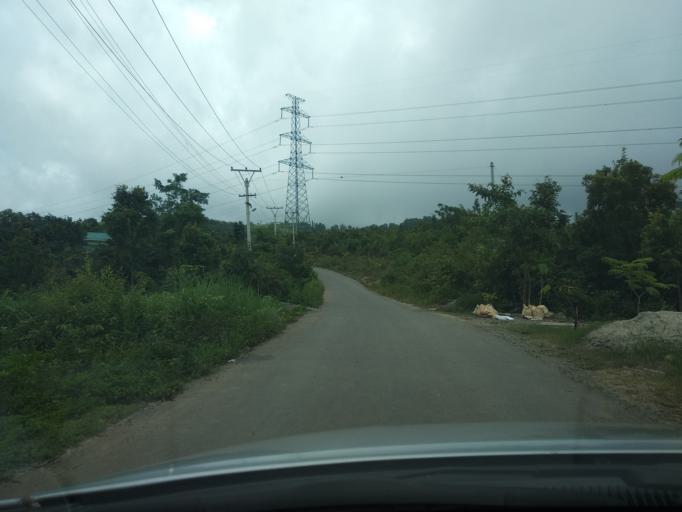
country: MM
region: Mandalay
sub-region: Pyin Oo Lwin District
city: Pyin Oo Lwin
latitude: 21.9134
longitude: 96.3843
